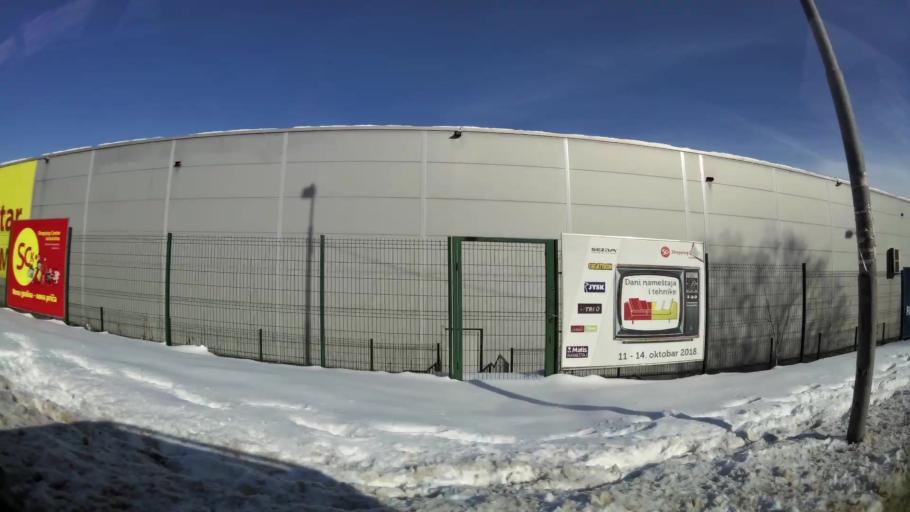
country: RS
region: Central Serbia
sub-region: Belgrade
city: Palilula
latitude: 44.8112
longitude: 20.5213
